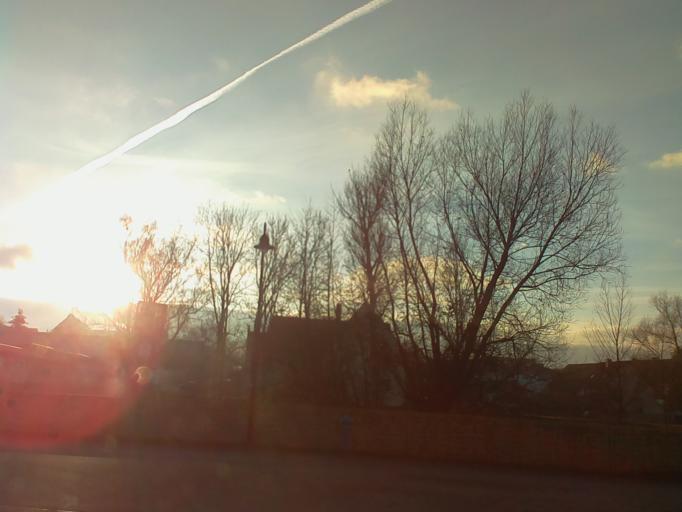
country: DE
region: Thuringia
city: Oppurg
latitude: 50.7130
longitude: 11.6533
